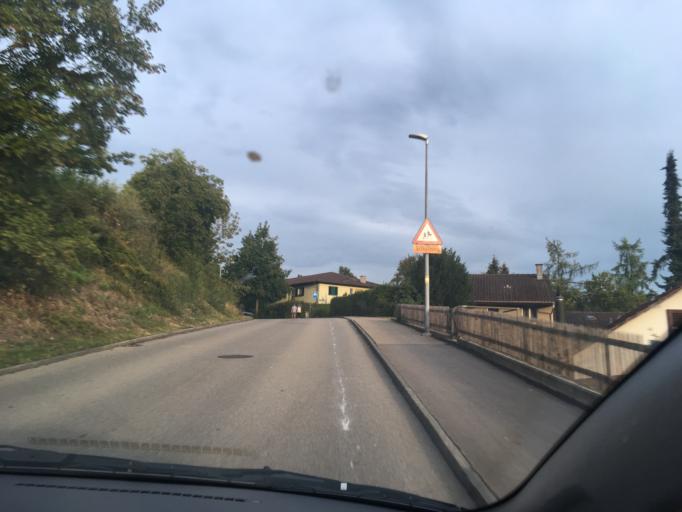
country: CH
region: Bern
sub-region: Bern-Mittelland District
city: Bern
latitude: 46.9731
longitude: 7.4360
